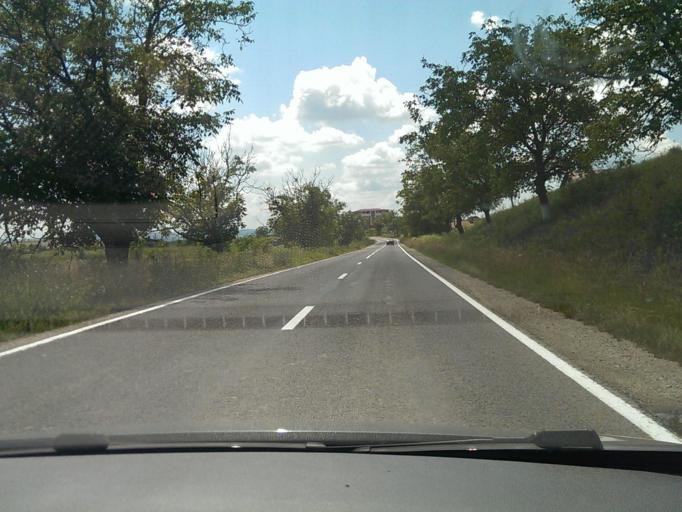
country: RO
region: Cluj
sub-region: Comuna Apahida
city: Apahida
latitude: 46.8030
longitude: 23.7690
